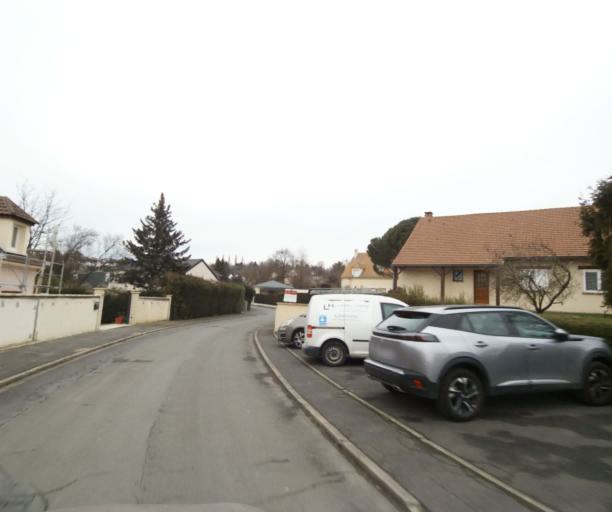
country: FR
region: Ile-de-France
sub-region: Departement de Seine-et-Marne
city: Dammartin-en-Goele
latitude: 49.0593
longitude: 2.6871
